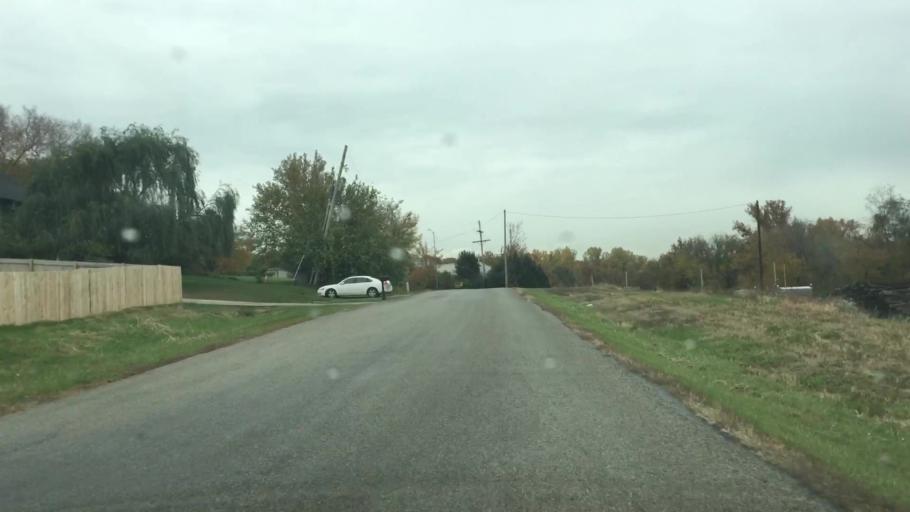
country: US
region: Kansas
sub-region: Wyandotte County
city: Edwardsville
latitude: 38.9987
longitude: -94.8229
